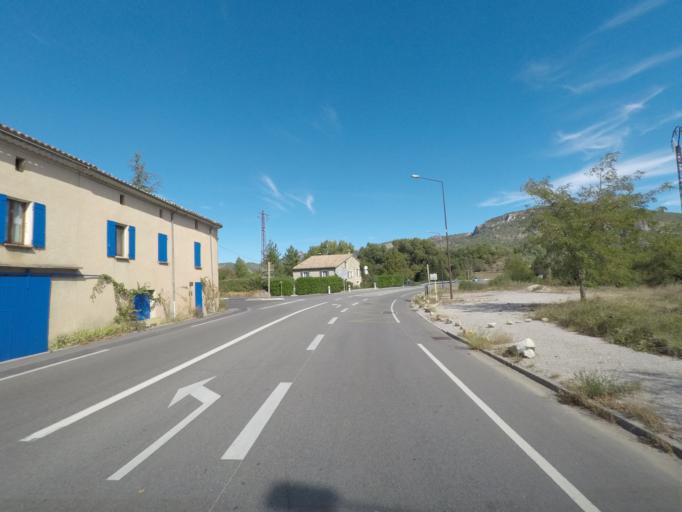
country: FR
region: Rhone-Alpes
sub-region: Departement de la Drome
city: Nyons
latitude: 44.3882
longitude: 5.1964
